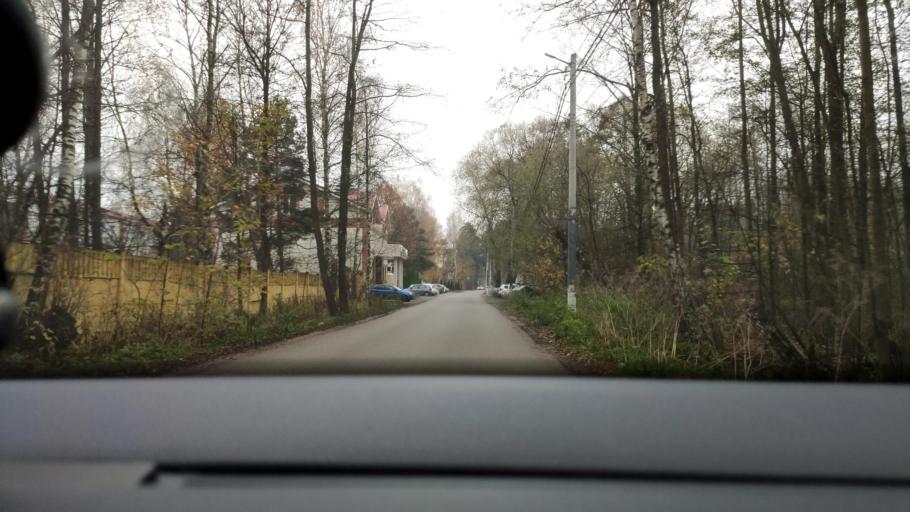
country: RU
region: Moskovskaya
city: Bykovo
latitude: 55.6409
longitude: 38.0977
